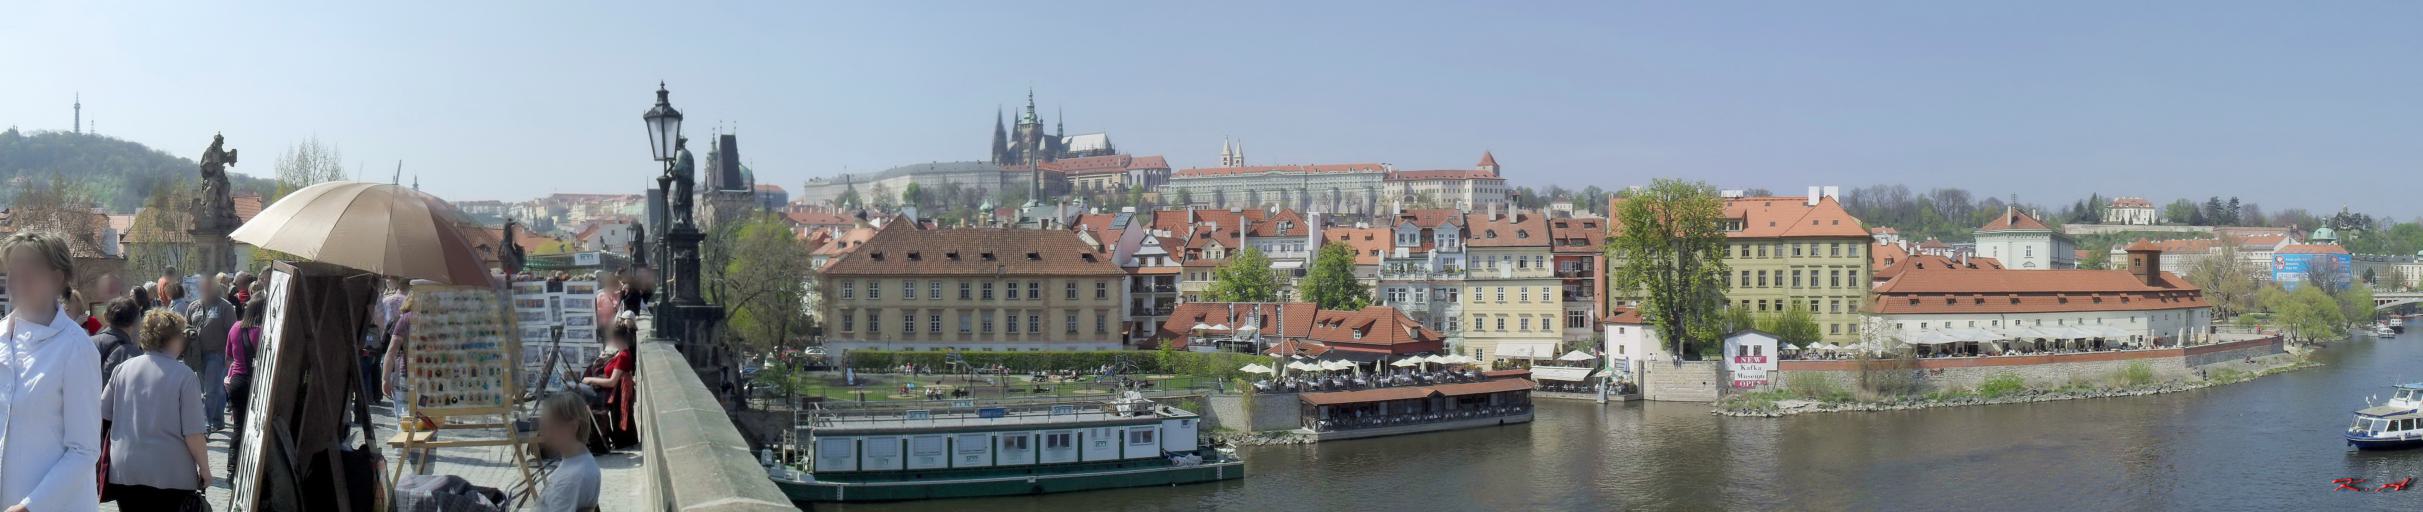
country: CZ
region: Praha
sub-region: Praha 1
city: Stare Mesto
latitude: 50.0864
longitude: 14.4133
